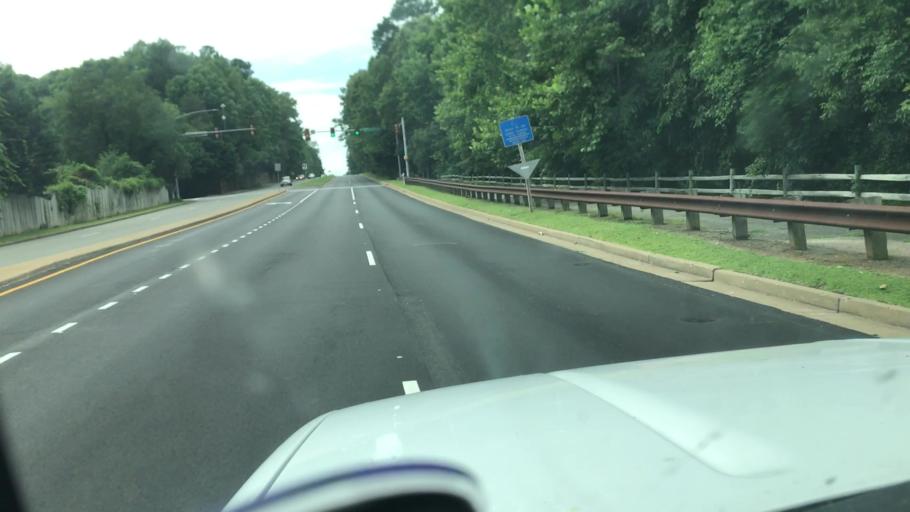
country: US
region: Virginia
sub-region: Henrico County
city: Short Pump
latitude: 37.6215
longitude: -77.5864
